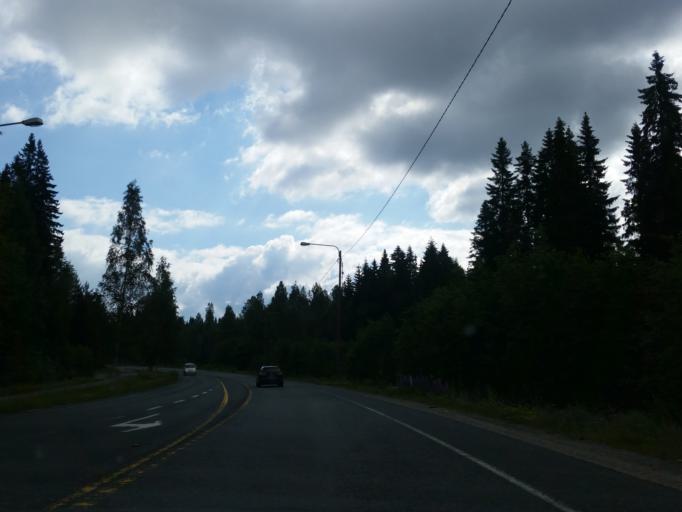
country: FI
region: Northern Savo
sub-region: Kuopio
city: Kuopio
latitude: 62.8384
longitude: 27.5647
